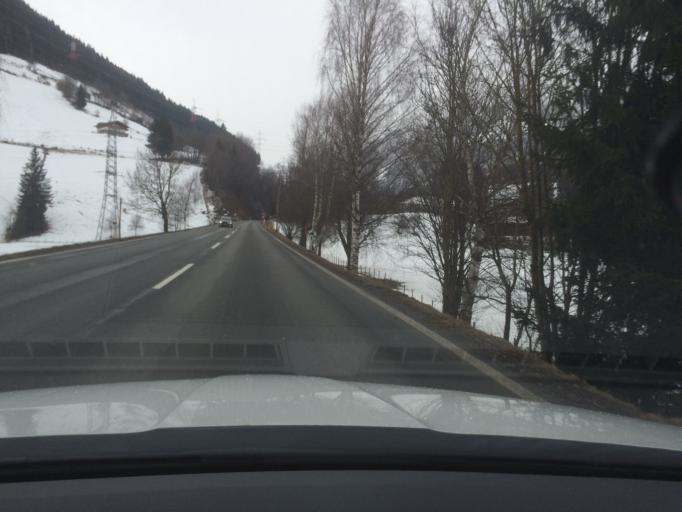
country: AT
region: Salzburg
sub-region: Politischer Bezirk Zell am See
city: Mittersill
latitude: 47.2759
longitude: 12.4878
